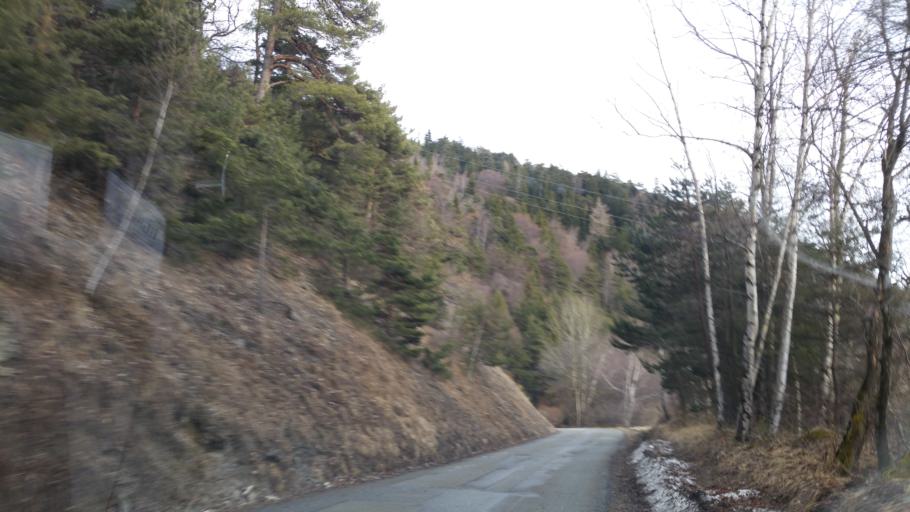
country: FR
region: Rhone-Alpes
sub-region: Departement de la Savoie
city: Villargondran
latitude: 45.2764
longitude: 6.3843
